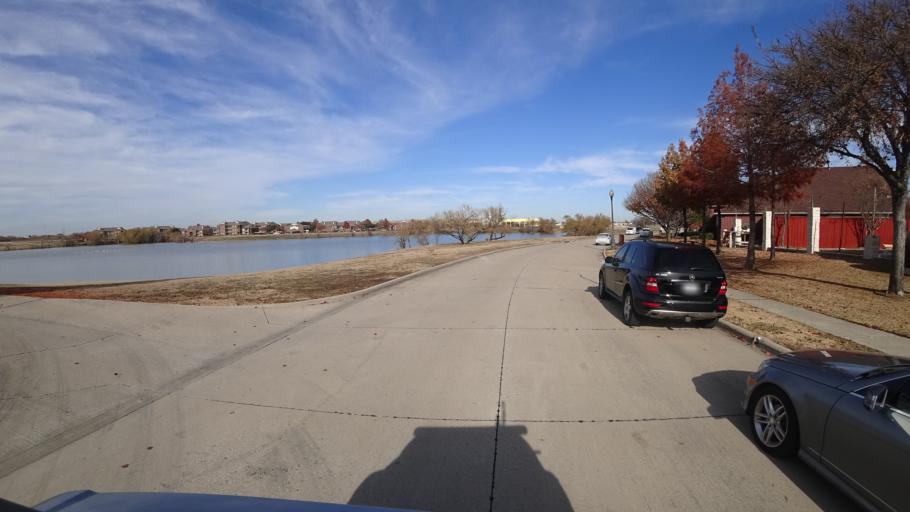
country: US
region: Texas
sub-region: Denton County
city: Lewisville
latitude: 33.0081
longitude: -96.9376
